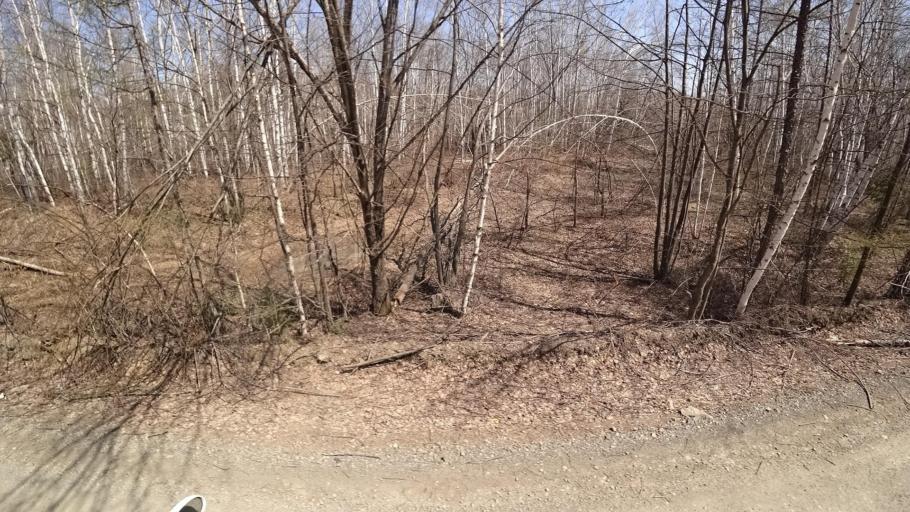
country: RU
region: Khabarovsk Krai
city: Khurba
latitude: 50.4130
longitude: 136.8421
